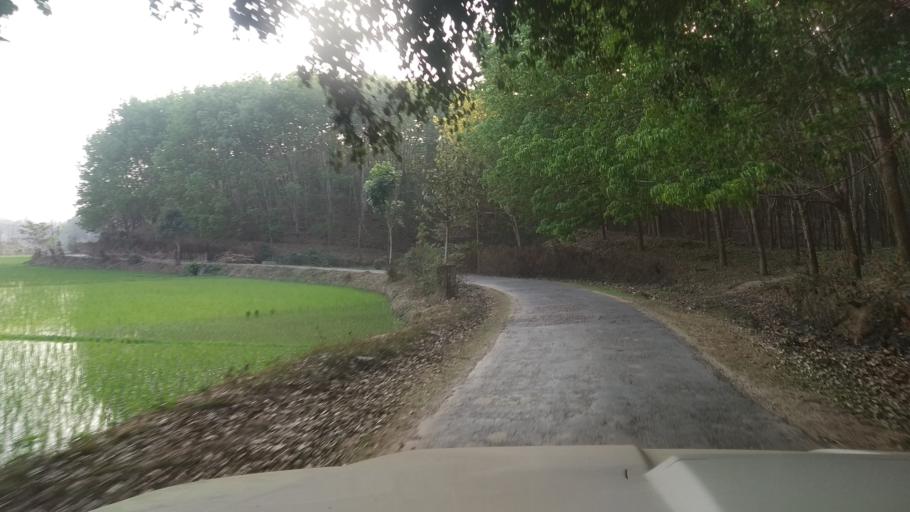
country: IN
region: Tripura
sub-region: West Tripura
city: Sonamura
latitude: 23.3432
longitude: 91.3206
